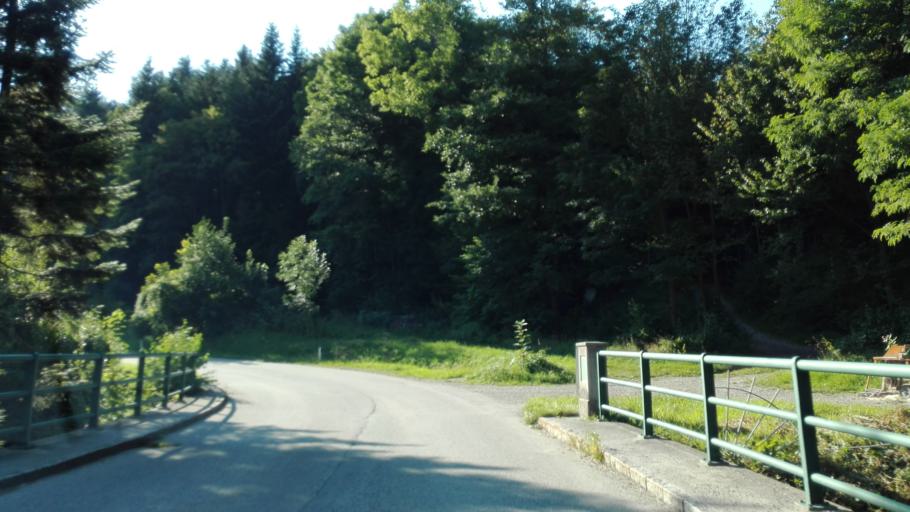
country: AT
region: Lower Austria
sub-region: Politischer Bezirk Sankt Polten
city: Stossing
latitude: 48.0851
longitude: 15.8482
